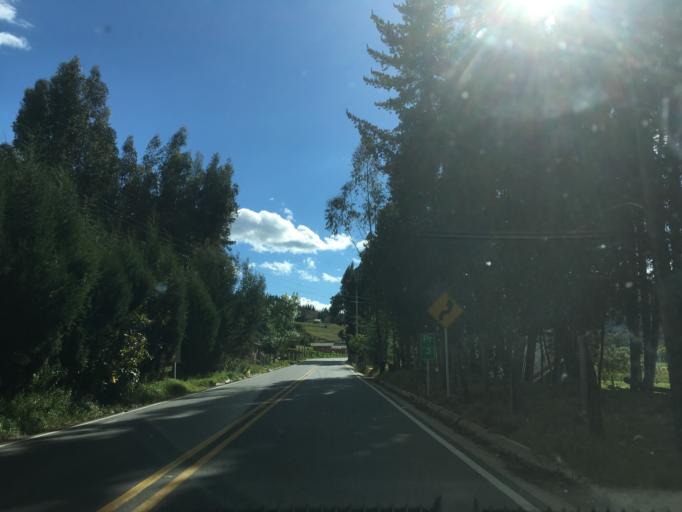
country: CO
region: Boyaca
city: Pesca
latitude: 5.5832
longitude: -73.0335
